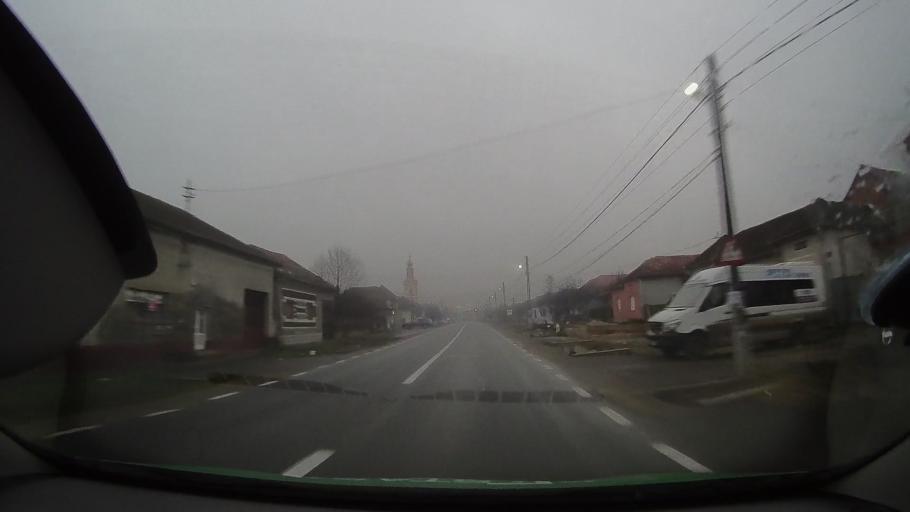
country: RO
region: Bihor
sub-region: Comuna Olcea
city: Calacea
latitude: 46.6387
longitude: 21.9559
